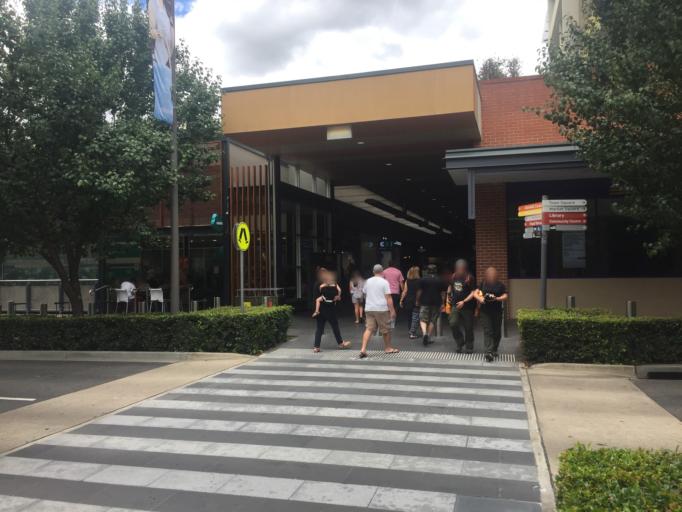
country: AU
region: New South Wales
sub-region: Blacktown
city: Rouse Hill
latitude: -33.6897
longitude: 150.9268
